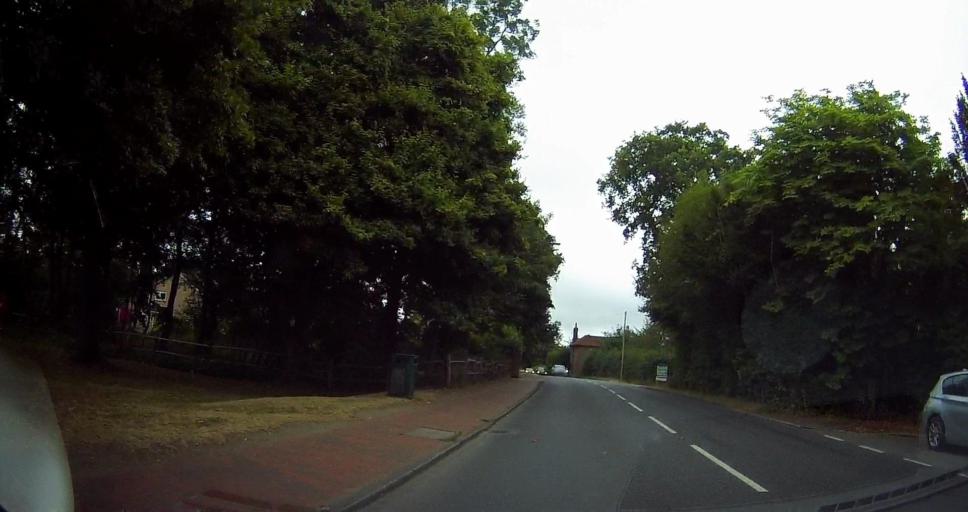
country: GB
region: England
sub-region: East Sussex
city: Wadhurst
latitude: 51.0647
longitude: 0.3341
